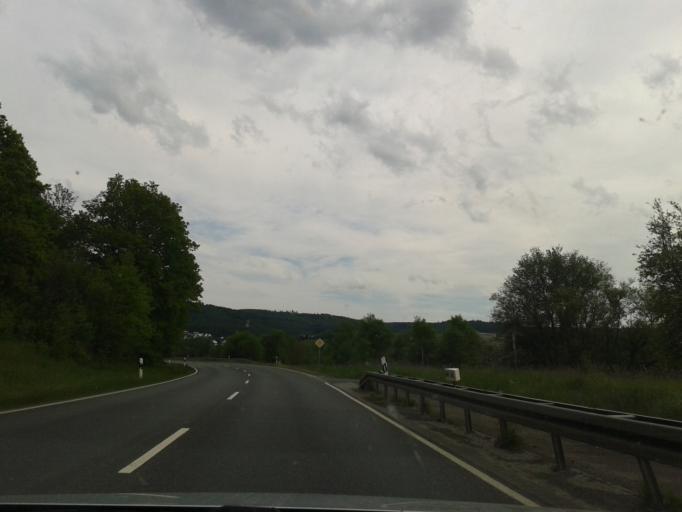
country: DE
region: Hesse
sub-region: Regierungsbezirk Giessen
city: Mittenaar
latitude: 50.6946
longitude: 8.3550
